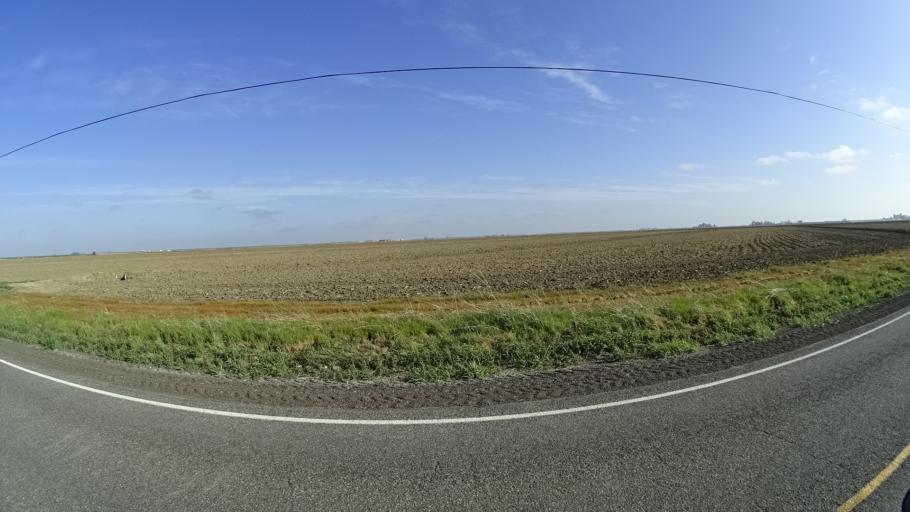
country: US
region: California
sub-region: Glenn County
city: Willows
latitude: 39.5821
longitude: -122.1108
